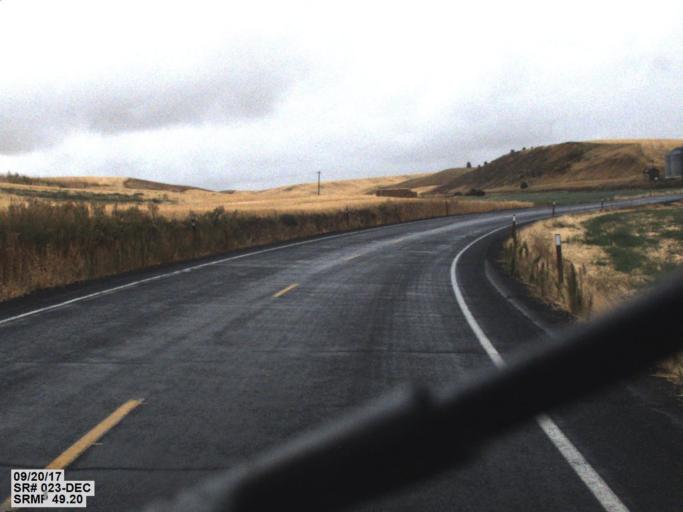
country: US
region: Washington
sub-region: Lincoln County
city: Davenport
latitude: 47.3585
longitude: -118.0425
